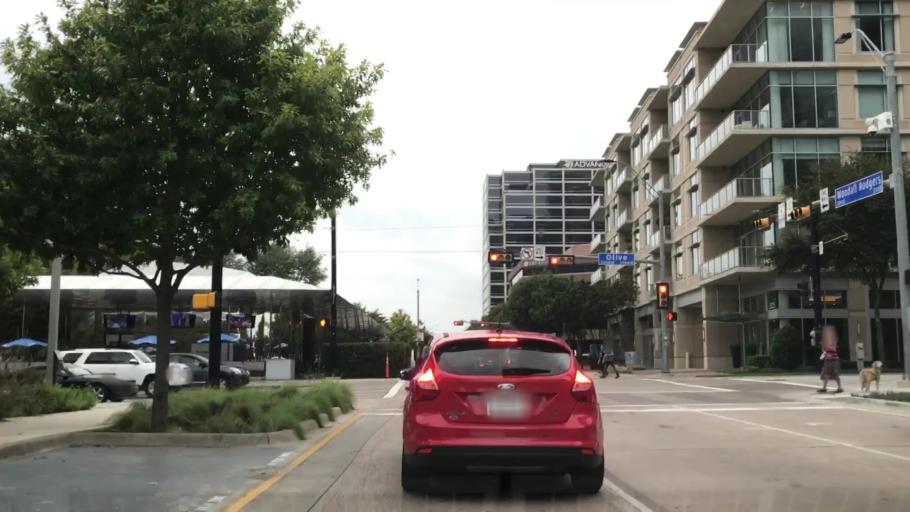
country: US
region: Texas
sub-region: Dallas County
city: Dallas
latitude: 32.7902
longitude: -96.8013
